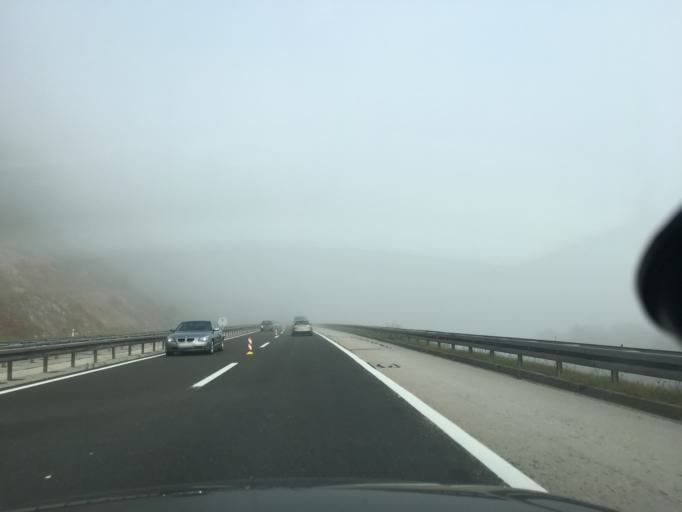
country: HR
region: Licko-Senjska
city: Otocac
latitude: 44.8546
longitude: 15.2246
